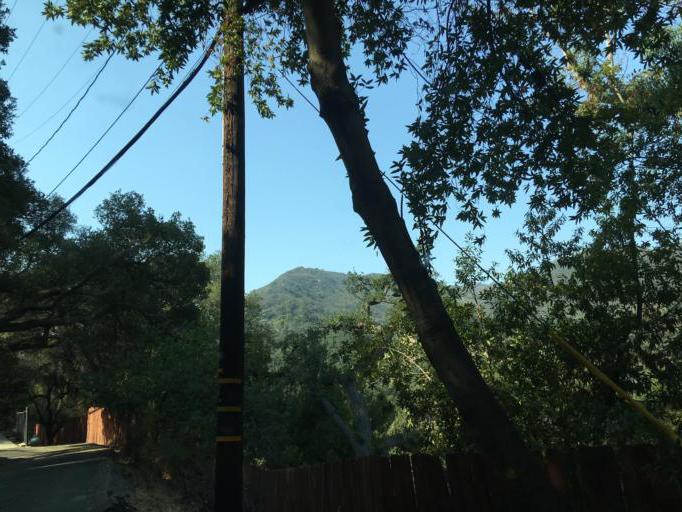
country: US
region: California
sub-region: Los Angeles County
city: Topanga
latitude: 34.0896
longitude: -118.6010
